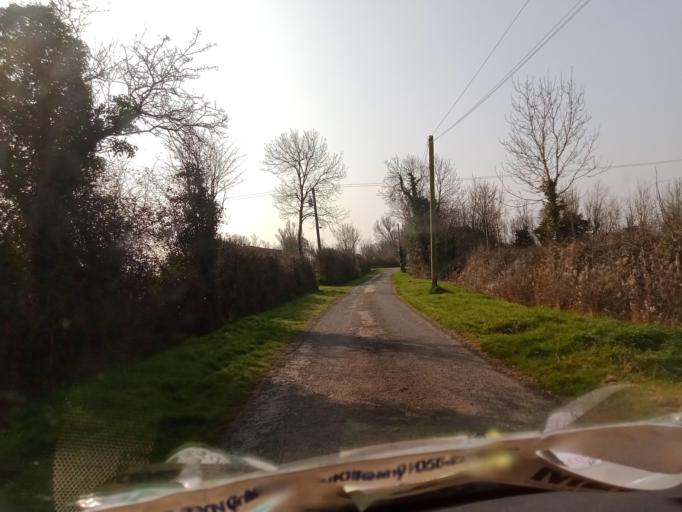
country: IE
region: Leinster
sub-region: Kilkenny
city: Callan
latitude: 52.5241
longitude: -7.4008
